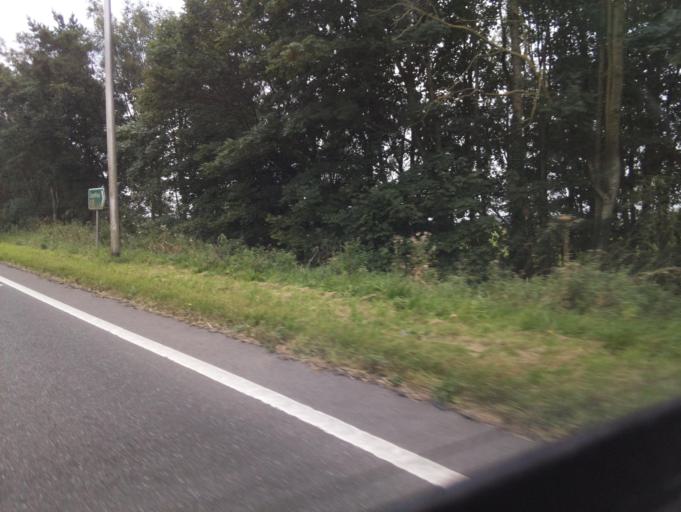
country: GB
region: Scotland
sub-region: Dumfries and Galloway
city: Locharbriggs
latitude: 55.0664
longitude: -3.5197
